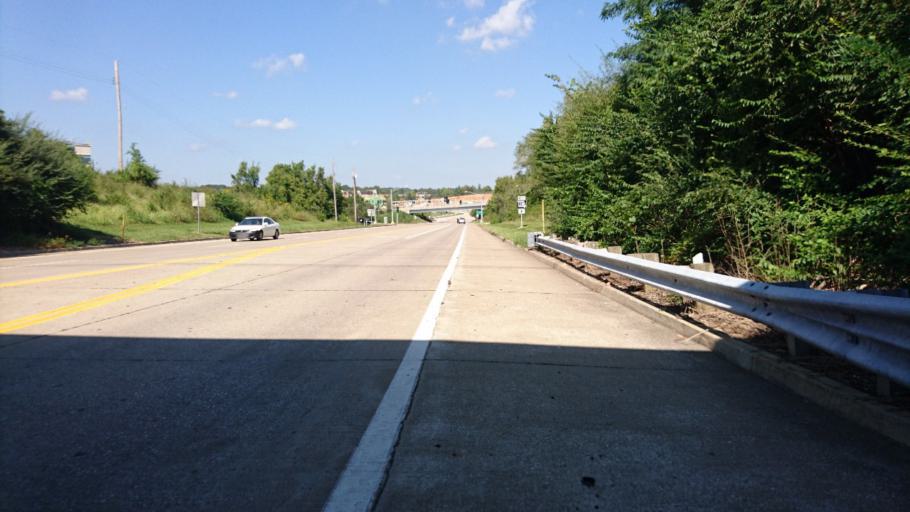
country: US
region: Missouri
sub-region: Saint Louis County
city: Town and Country
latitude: 38.6016
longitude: -90.4552
